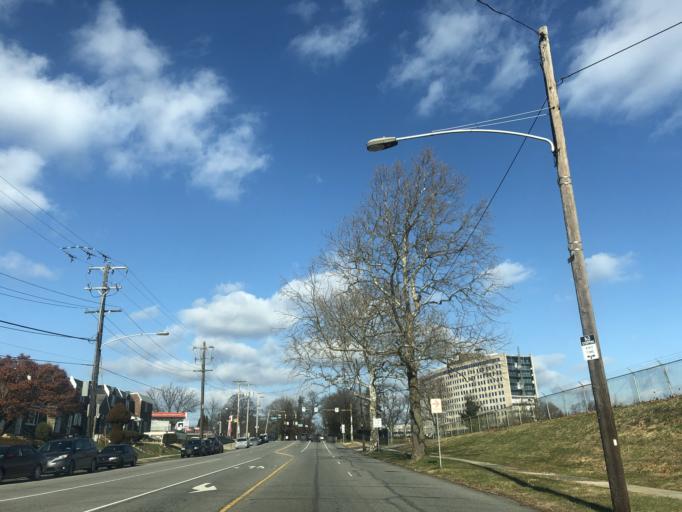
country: US
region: Pennsylvania
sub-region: Montgomery County
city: Bala-Cynwyd
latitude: 40.0024
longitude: -75.2202
